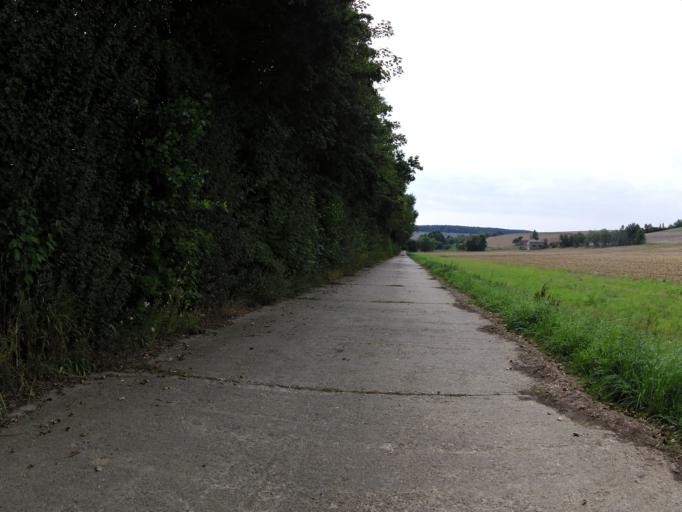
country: DE
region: Bavaria
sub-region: Regierungsbezirk Unterfranken
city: Kleinrinderfeld
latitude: 49.7046
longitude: 9.8373
